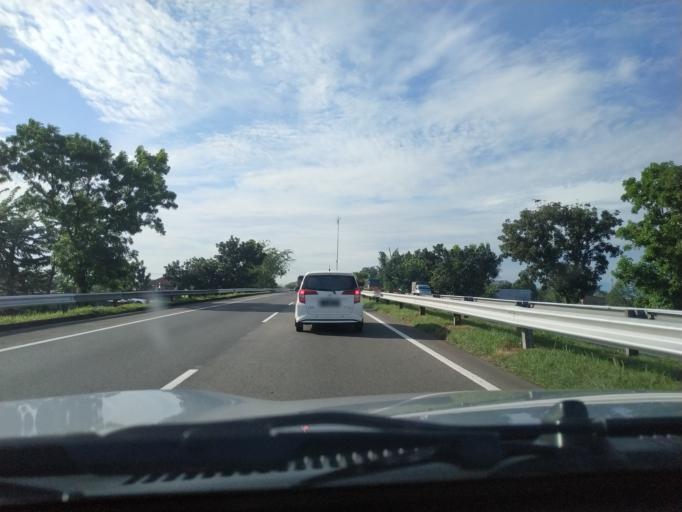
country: ID
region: North Sumatra
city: Medan
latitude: 3.5745
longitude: 98.7253
